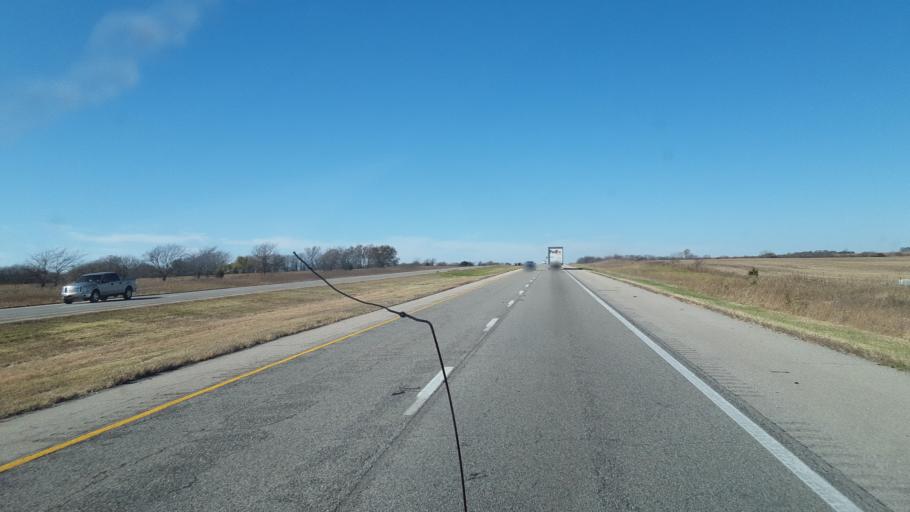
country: US
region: Kansas
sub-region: Osage County
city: Lyndon
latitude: 38.4265
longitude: -95.7555
